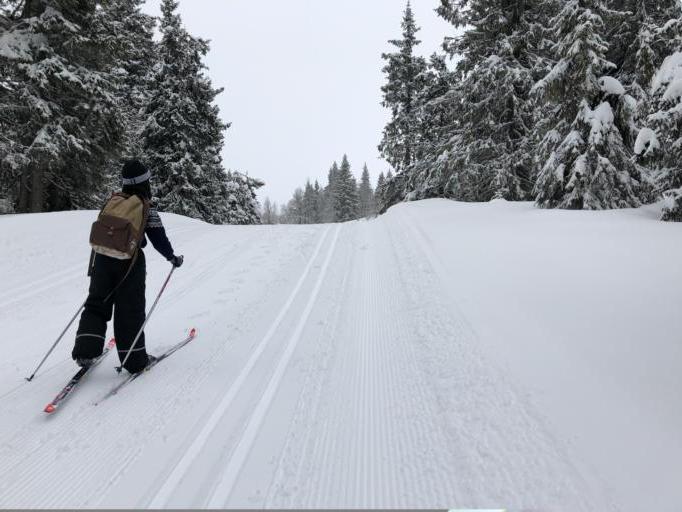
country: NO
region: Oppland
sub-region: Gausdal
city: Segalstad bru
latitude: 61.3205
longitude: 10.0577
